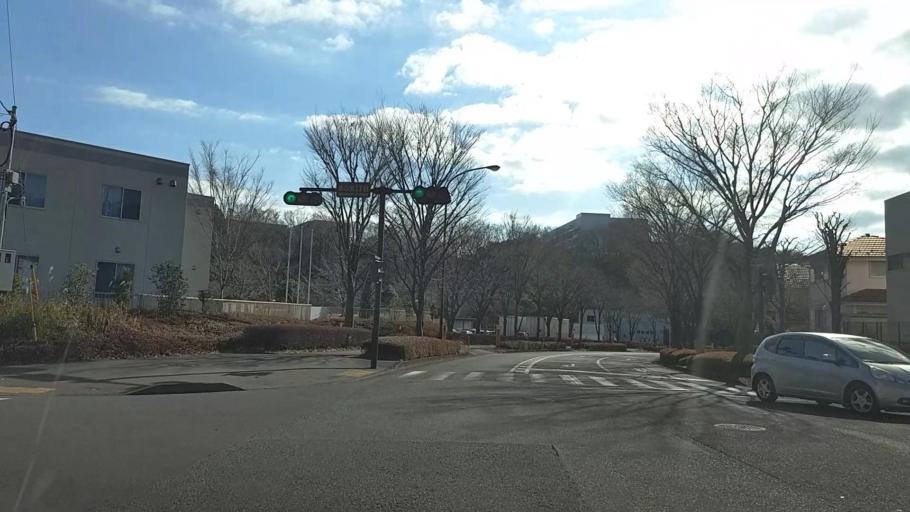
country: JP
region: Kanagawa
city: Atsugi
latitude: 35.4495
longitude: 139.3103
